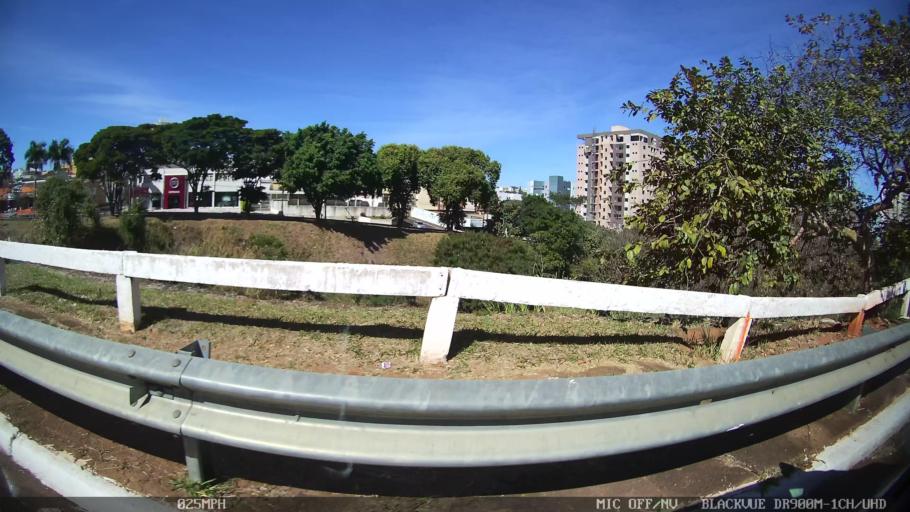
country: BR
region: Sao Paulo
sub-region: Franca
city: Franca
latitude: -20.5489
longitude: -47.4029
